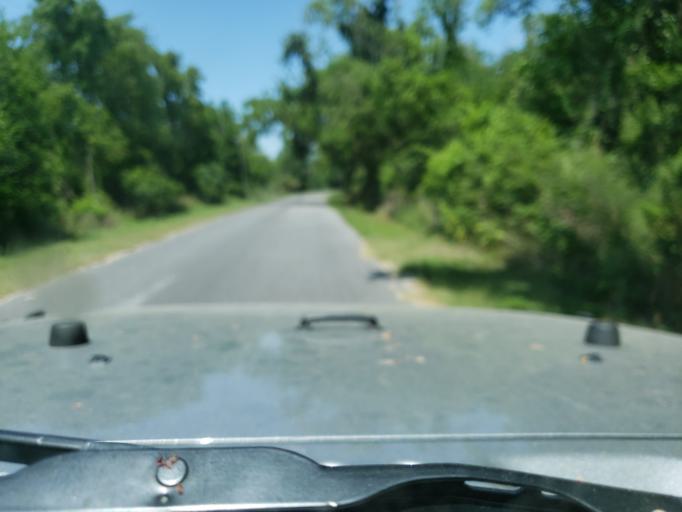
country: US
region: Georgia
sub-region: Chatham County
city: Thunderbolt
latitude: 32.0785
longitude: -81.0415
